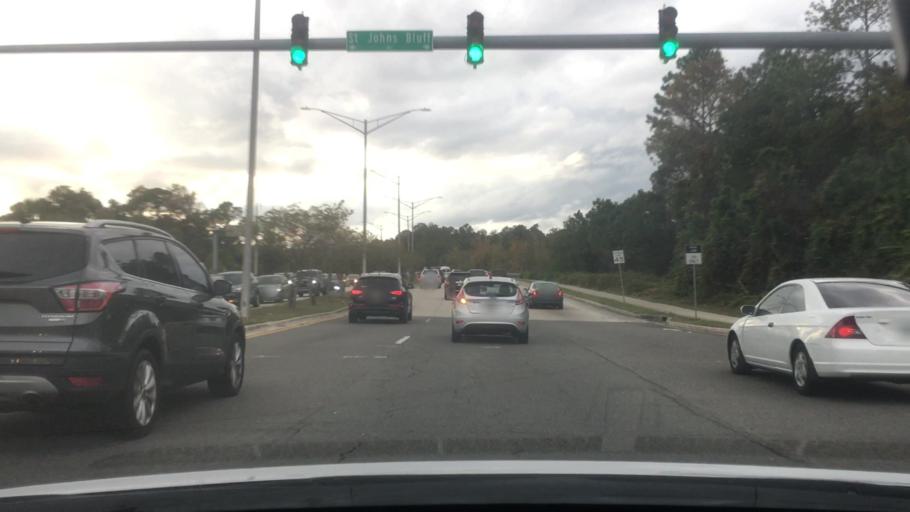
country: US
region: Florida
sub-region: Duval County
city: Jacksonville Beach
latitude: 30.2680
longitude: -81.5237
